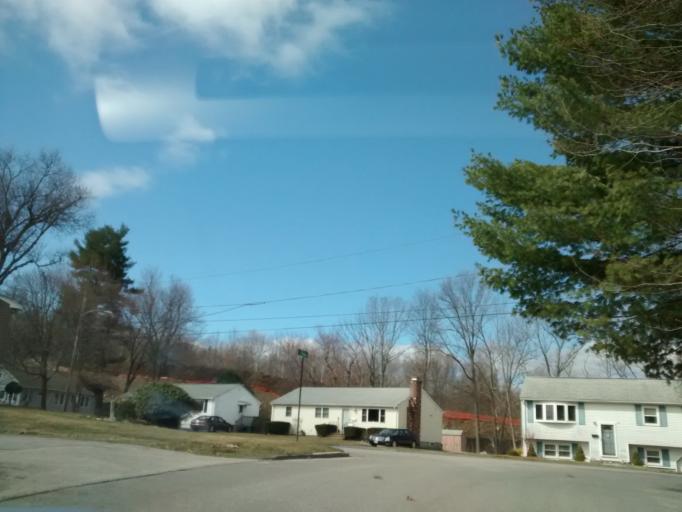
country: US
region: Massachusetts
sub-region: Worcester County
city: Worcester
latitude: 42.2931
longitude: -71.8199
